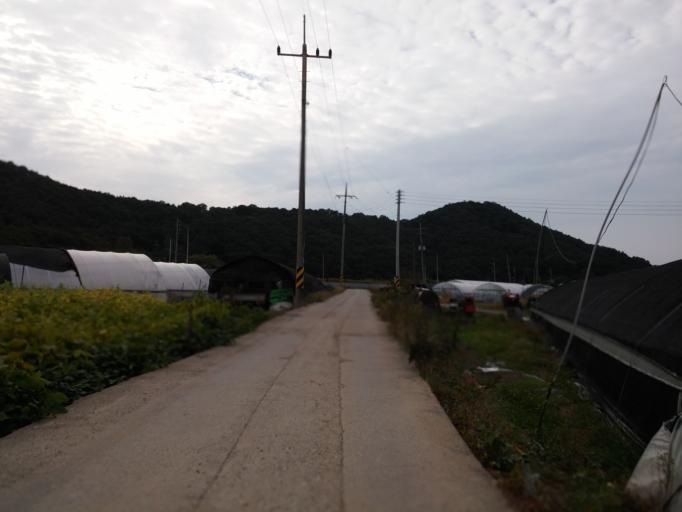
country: KR
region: Chungcheongnam-do
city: Yonmu
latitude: 36.1553
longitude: 127.2057
